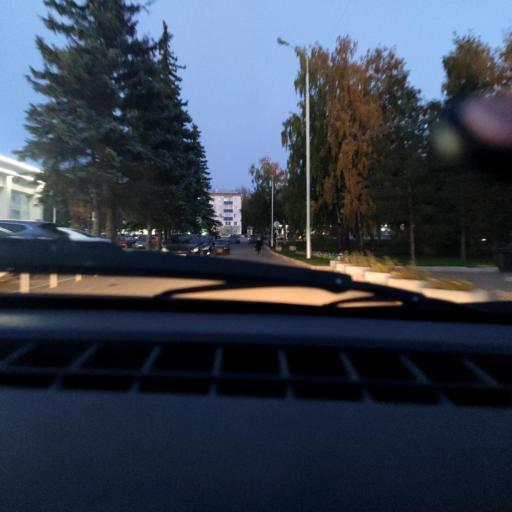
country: RU
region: Bashkortostan
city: Ufa
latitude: 54.7738
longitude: 56.0255
